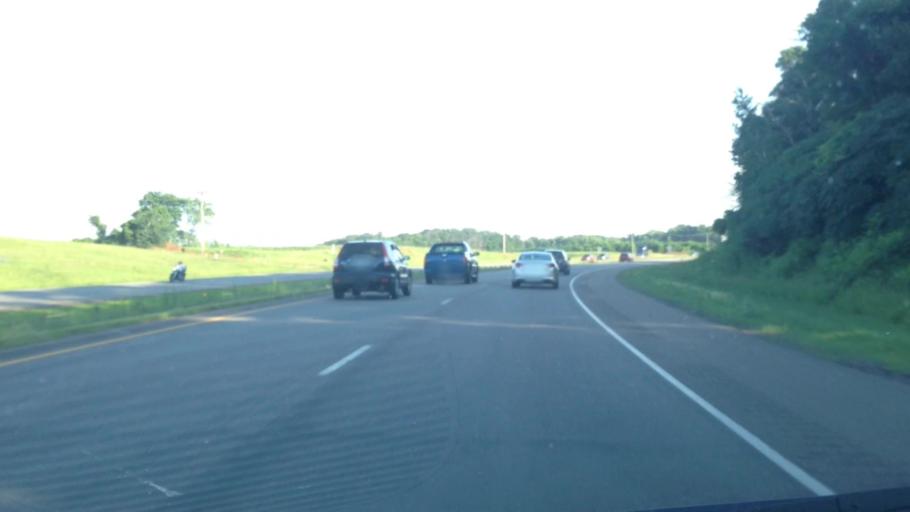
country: US
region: Minnesota
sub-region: Sherburne County
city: Zimmerman
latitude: 45.3940
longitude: -93.5620
